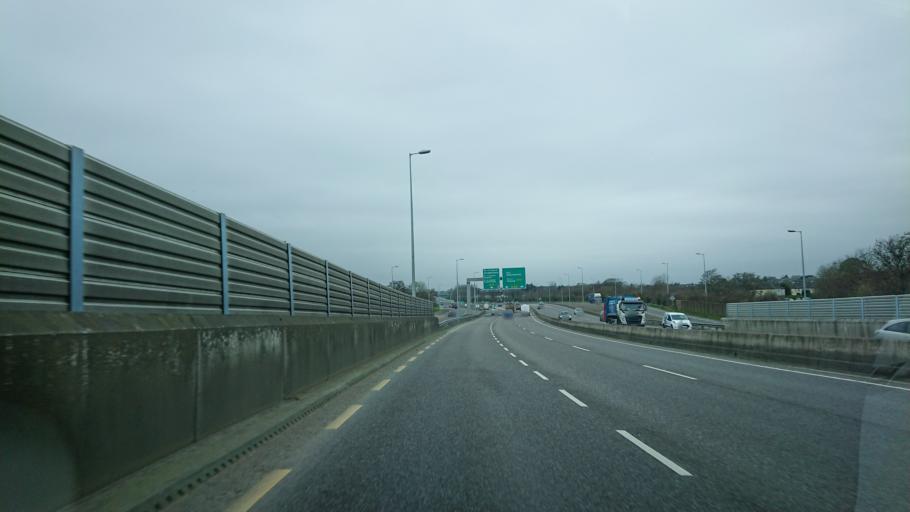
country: IE
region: Munster
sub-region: County Cork
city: Cork
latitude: 51.8759
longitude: -8.5092
